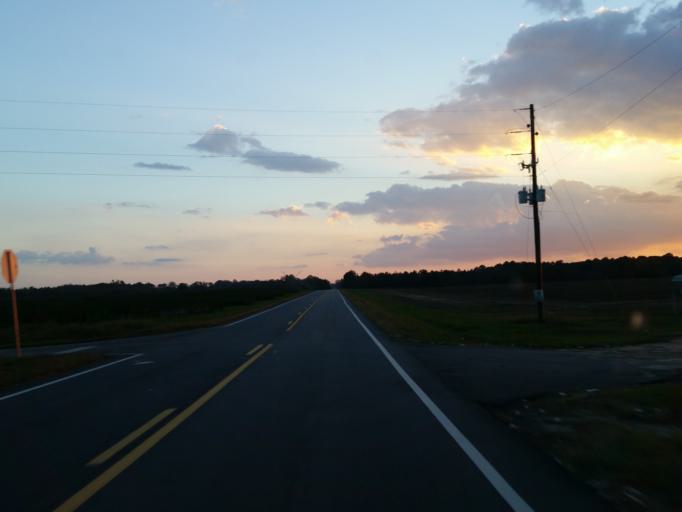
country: US
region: Georgia
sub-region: Pulaski County
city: Hawkinsville
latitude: 32.1973
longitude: -83.5793
